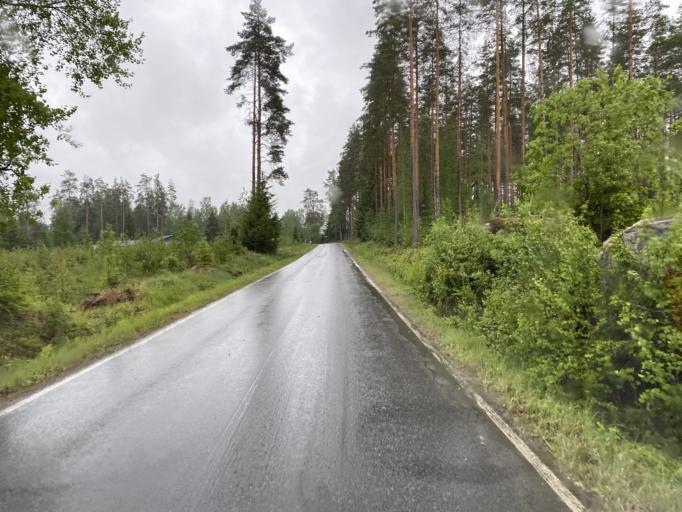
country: FI
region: Haeme
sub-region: Forssa
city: Humppila
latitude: 61.0692
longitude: 23.3181
